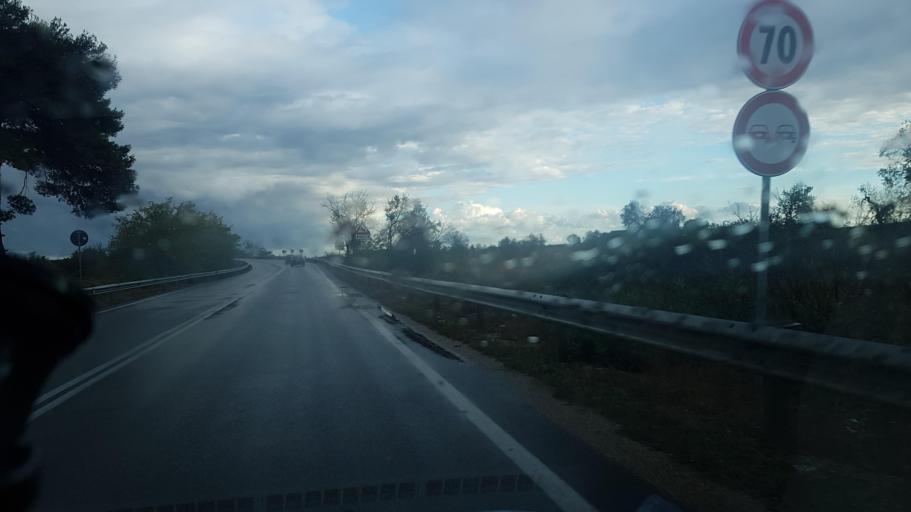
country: IT
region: Apulia
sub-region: Provincia di Lecce
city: Surbo
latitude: 40.3822
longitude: 18.1117
